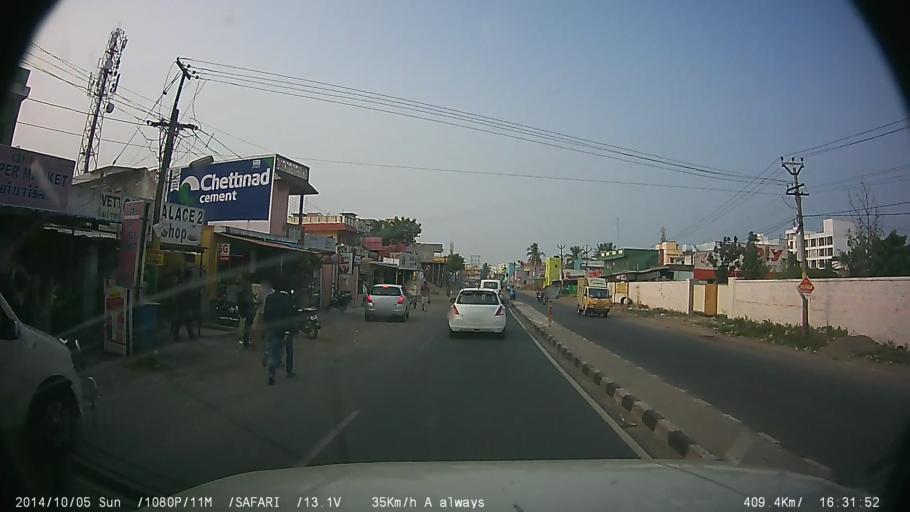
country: IN
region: Tamil Nadu
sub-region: Kancheepuram
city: Vengavasal
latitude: 12.8022
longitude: 80.2237
